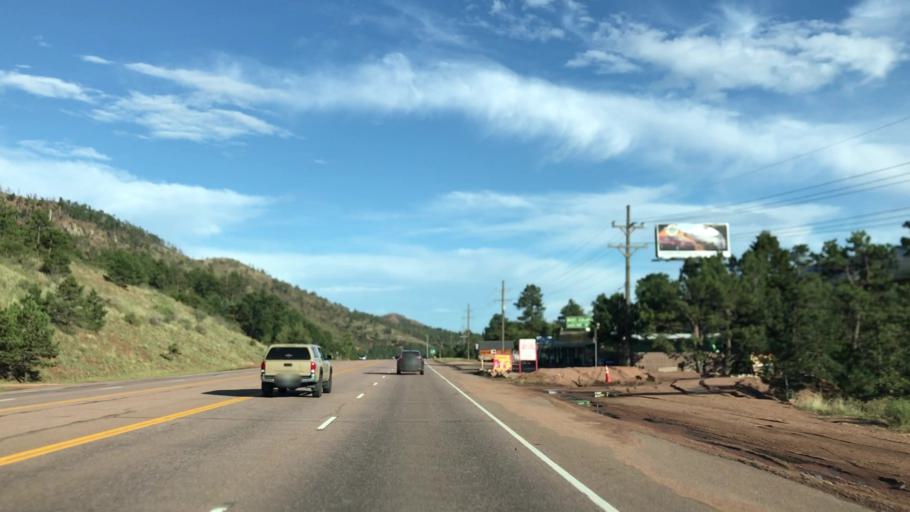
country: US
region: Colorado
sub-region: El Paso County
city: Cascade-Chipita Park
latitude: 38.9155
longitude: -104.9812
